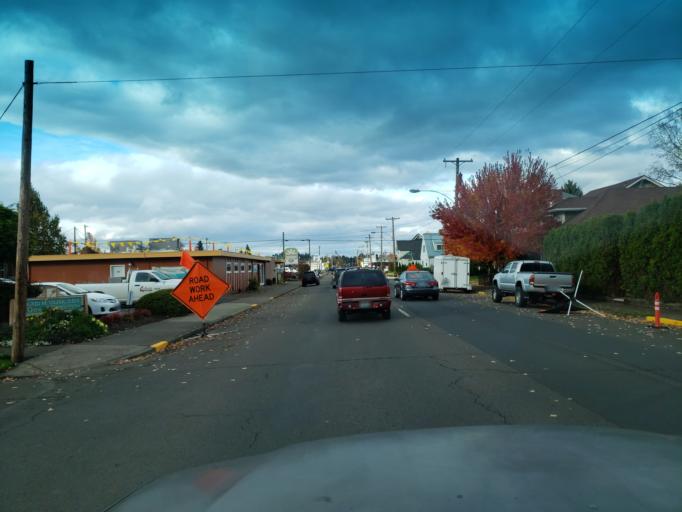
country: US
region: Oregon
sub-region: Yamhill County
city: McMinnville
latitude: 45.2135
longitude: -123.1980
